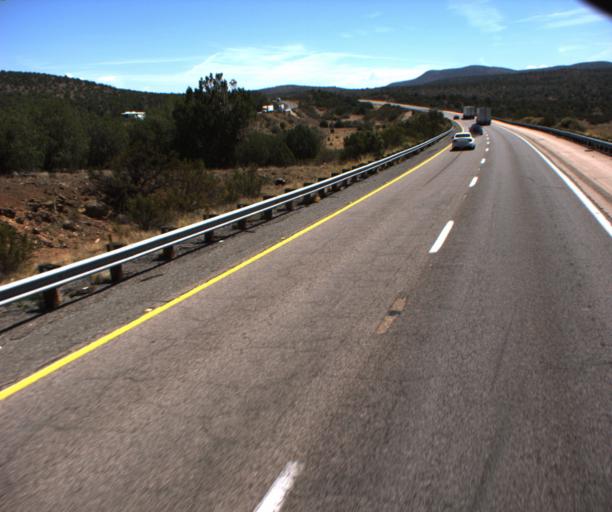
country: US
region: Arizona
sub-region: Mohave County
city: Peach Springs
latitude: 35.1888
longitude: -113.3209
